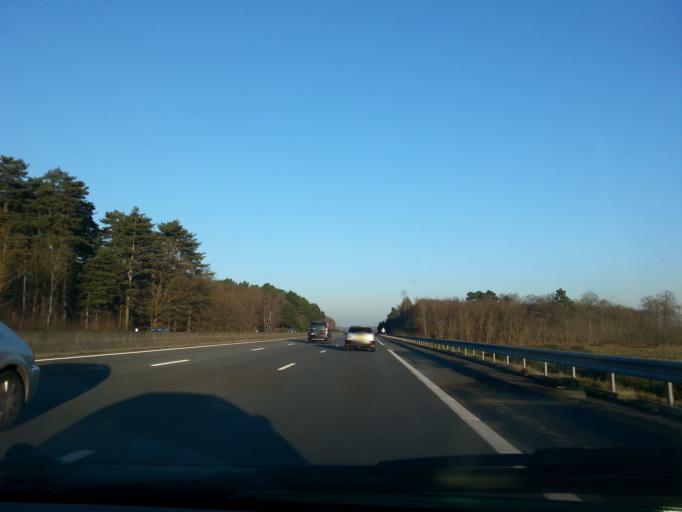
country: FR
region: Pays de la Loire
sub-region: Departement de la Sarthe
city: Tuffe
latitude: 48.0945
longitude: 0.5220
